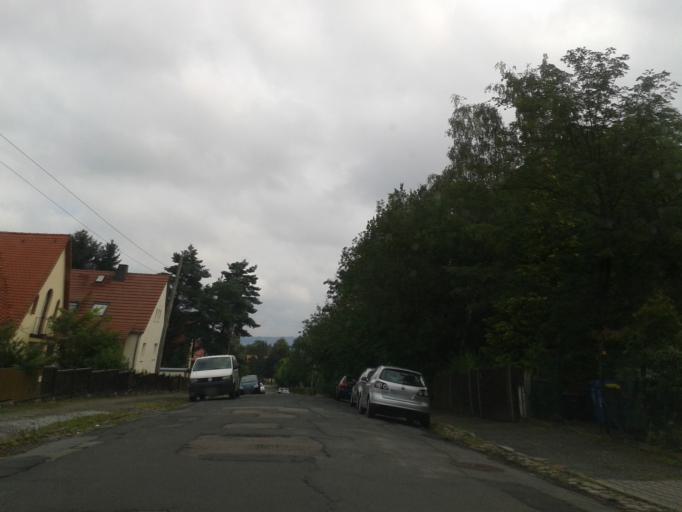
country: DE
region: Saxony
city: Bannewitz
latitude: 51.0121
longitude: 13.7515
